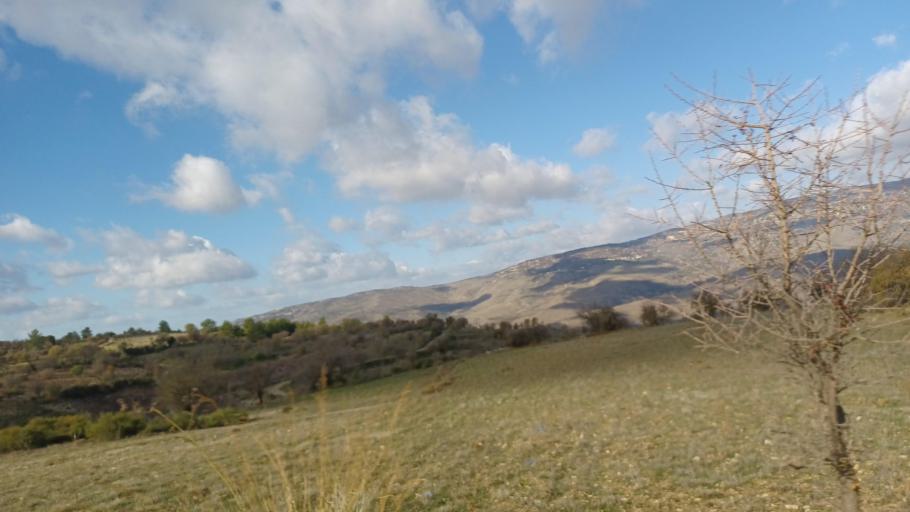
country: CY
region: Limassol
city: Pachna
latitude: 34.8561
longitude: 32.6910
